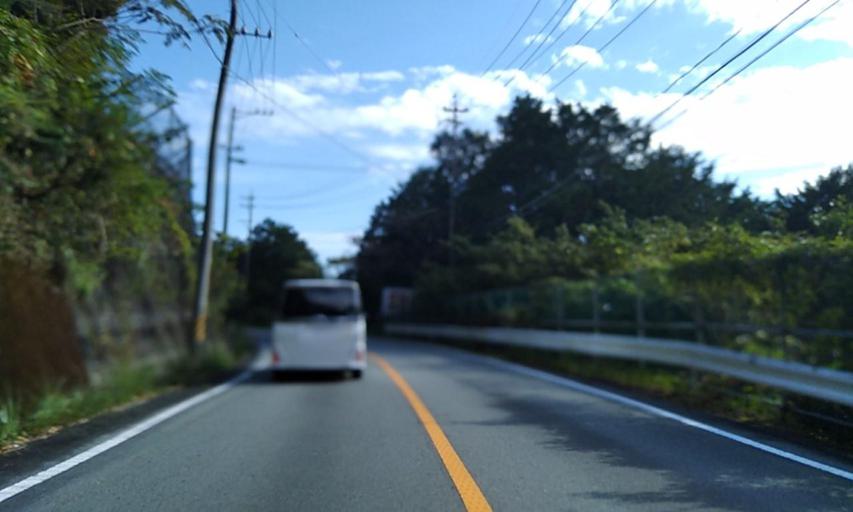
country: JP
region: Mie
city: Owase
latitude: 34.2179
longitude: 136.3847
